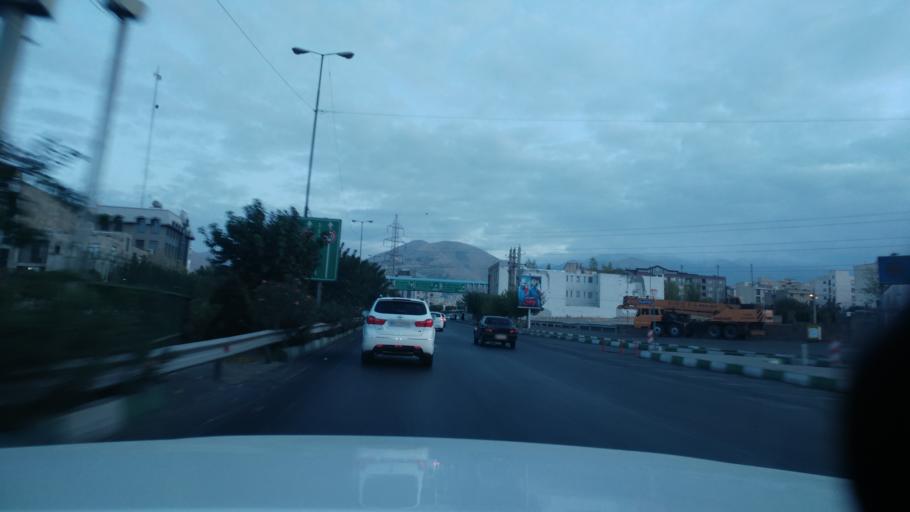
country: IR
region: Tehran
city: Tehran
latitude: 35.7460
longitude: 51.3144
